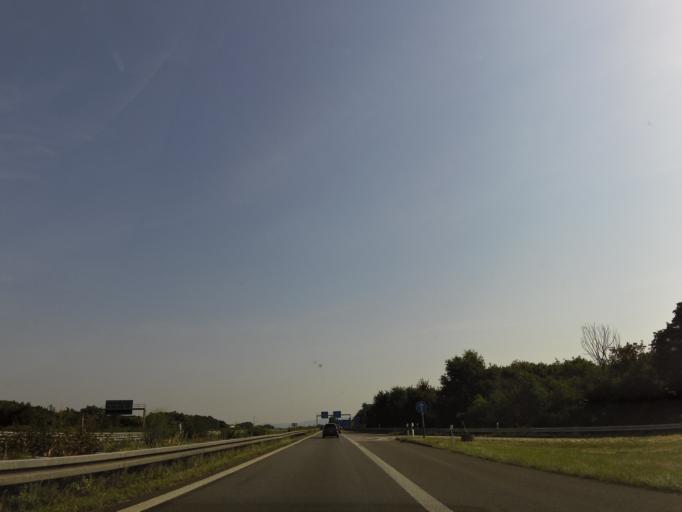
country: DE
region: Baden-Wuerttemberg
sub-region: Karlsruhe Region
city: Sankt Leon-Rot
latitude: 49.2792
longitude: 8.6199
